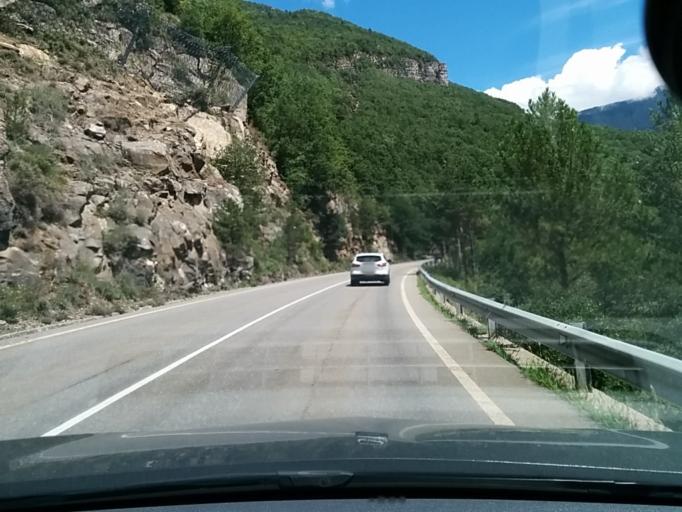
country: ES
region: Aragon
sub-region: Provincia de Huesca
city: Bielsa
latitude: 42.5866
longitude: 0.2237
